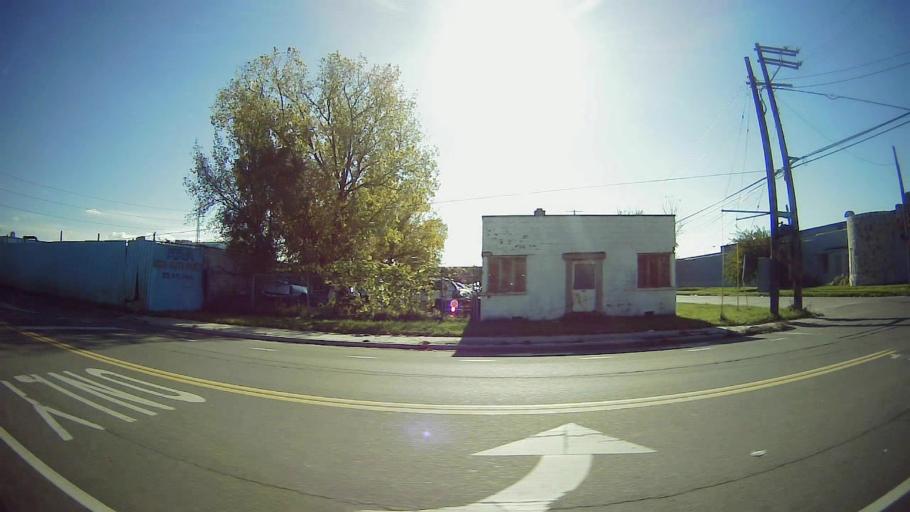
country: US
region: Michigan
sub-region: Wayne County
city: Dearborn
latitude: 42.3657
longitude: -83.1836
